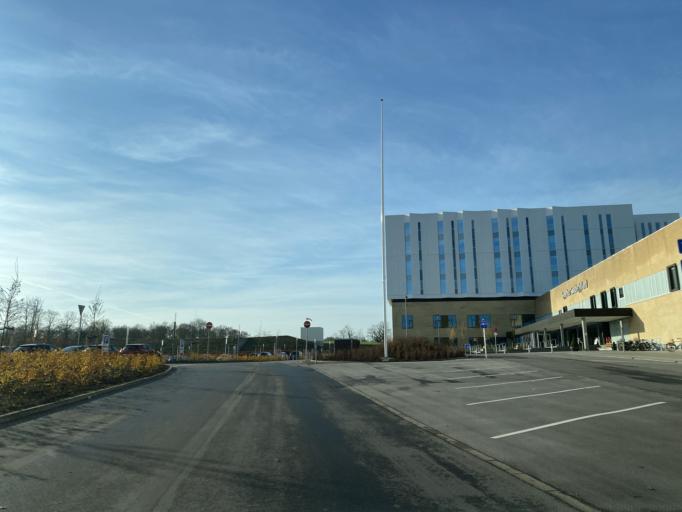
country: DK
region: South Denmark
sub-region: Aabenraa Kommune
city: Aabenraa
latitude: 55.0623
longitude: 9.3803
